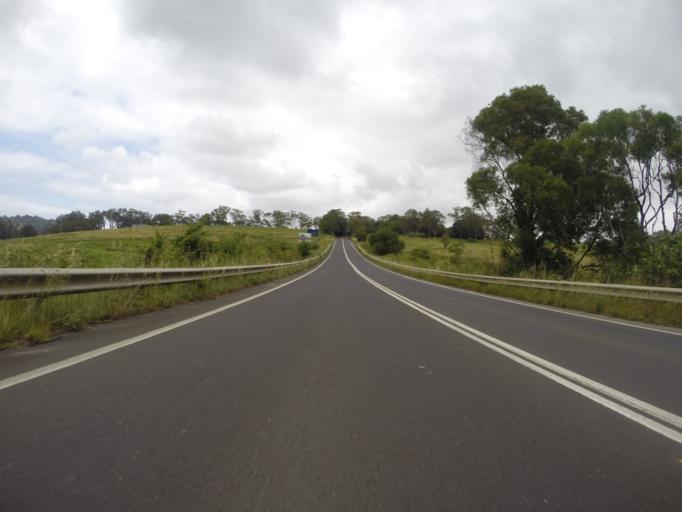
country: AU
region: New South Wales
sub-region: Shoalhaven Shire
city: Berry
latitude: -34.7532
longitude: 150.7499
